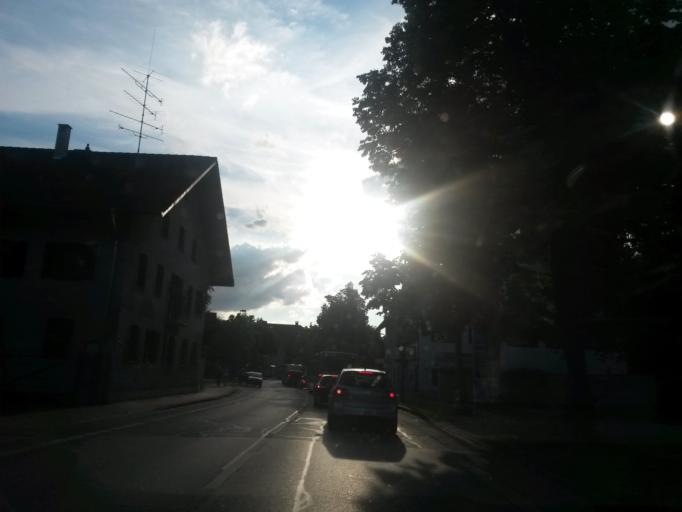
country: DE
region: Bavaria
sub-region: Upper Bavaria
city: Neubiberg
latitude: 48.0997
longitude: 11.6323
